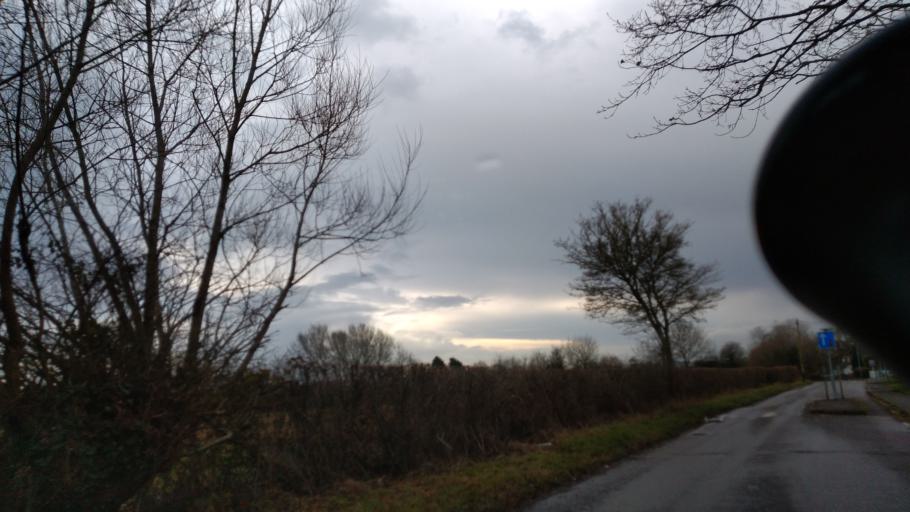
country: GB
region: England
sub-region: Borough of Swindon
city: Highworth
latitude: 51.5941
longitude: -1.7251
